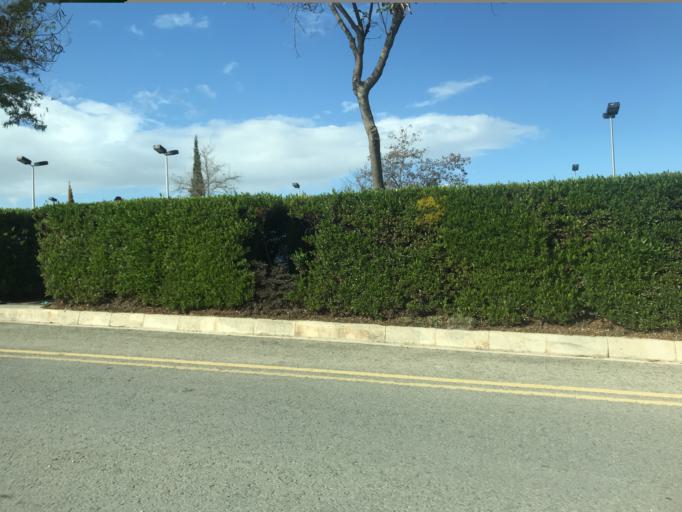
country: CY
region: Lefkosia
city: Geri
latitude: 35.1462
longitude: 33.4091
